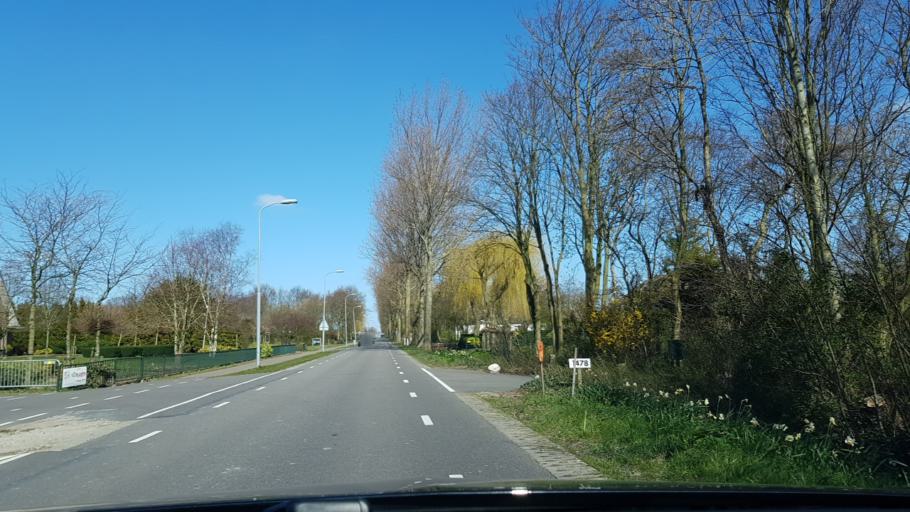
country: NL
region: South Holland
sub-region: Gemeente Hillegom
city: Hillegom
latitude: 52.2856
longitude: 4.6242
